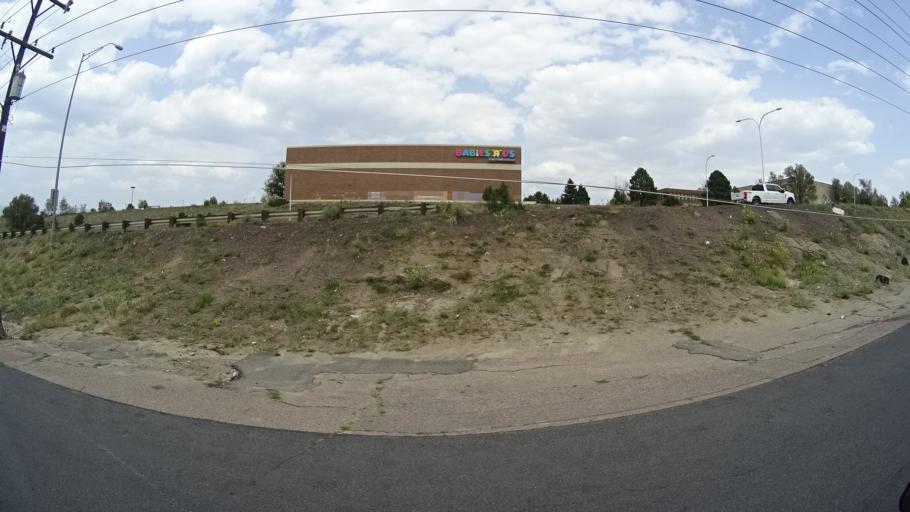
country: US
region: Colorado
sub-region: El Paso County
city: Colorado Springs
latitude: 38.8394
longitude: -104.7614
